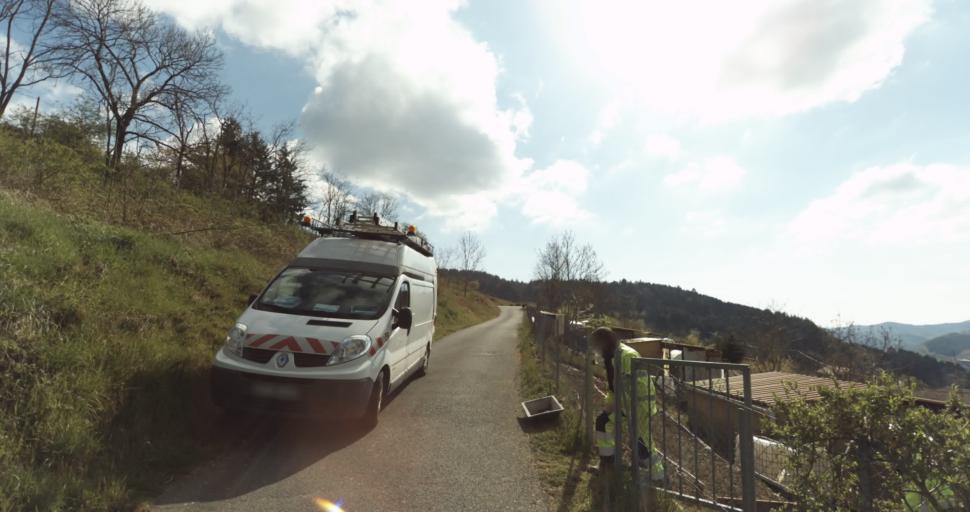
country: FR
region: Rhone-Alpes
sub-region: Departement du Rhone
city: Tarare
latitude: 45.8986
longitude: 4.4488
